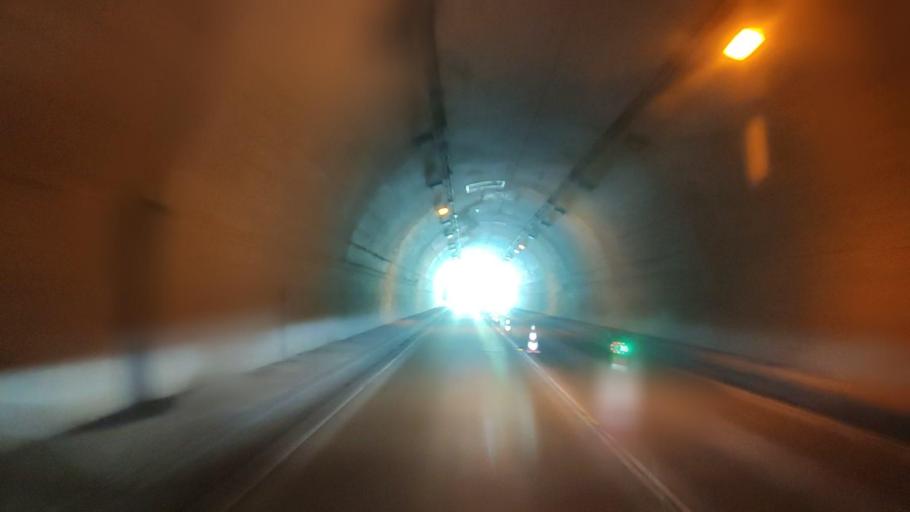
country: JP
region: Nara
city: Yoshino-cho
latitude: 34.2842
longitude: 136.0041
